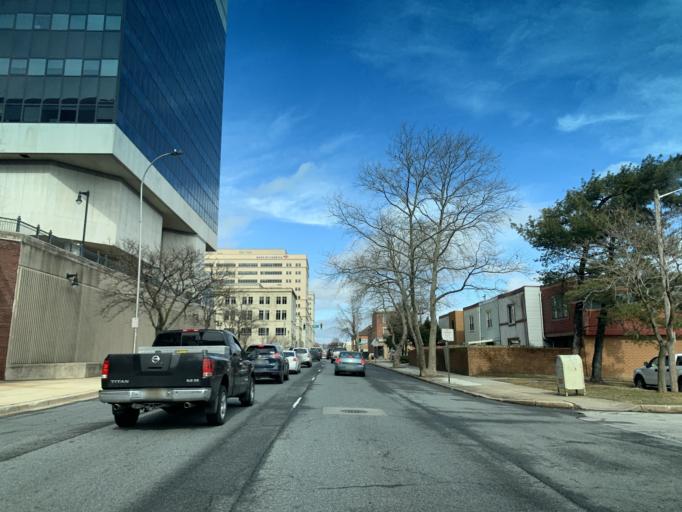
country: US
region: Delaware
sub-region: New Castle County
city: Wilmington
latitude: 39.7428
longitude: -75.5461
